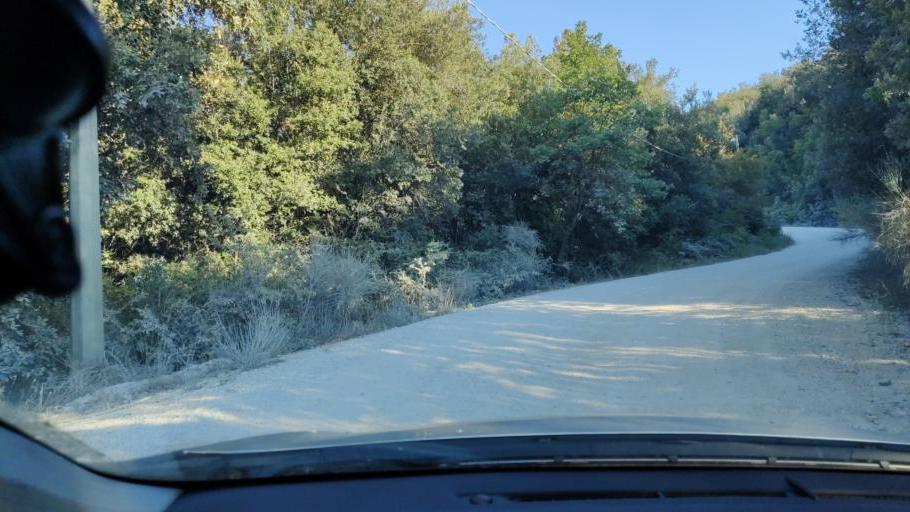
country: IT
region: Umbria
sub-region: Provincia di Terni
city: Amelia
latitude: 42.5404
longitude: 12.3828
